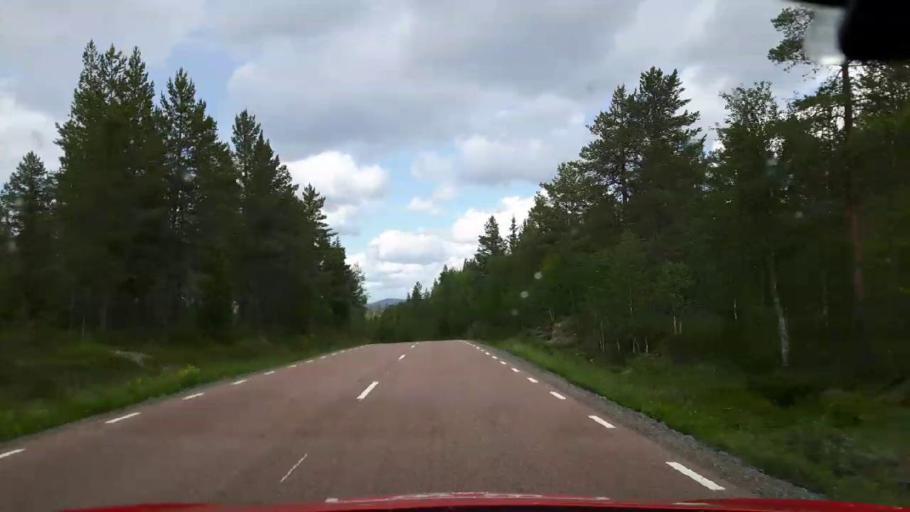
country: SE
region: Jaemtland
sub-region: Krokoms Kommun
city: Valla
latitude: 63.9413
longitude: 14.2239
